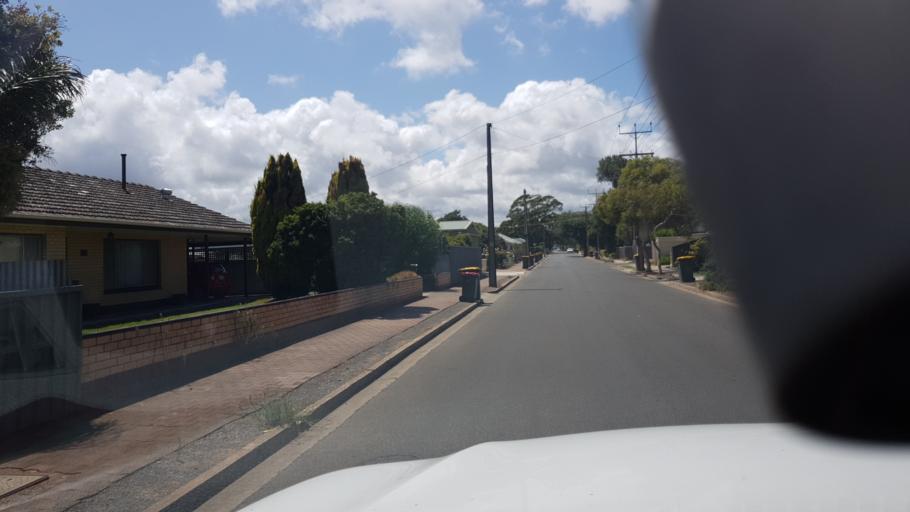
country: AU
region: South Australia
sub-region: Adelaide
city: Brighton
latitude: -35.0134
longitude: 138.5280
